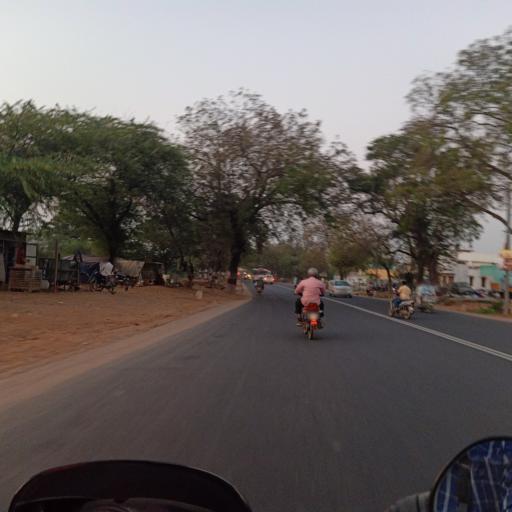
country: IN
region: Telangana
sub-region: Rangareddi
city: Secunderabad
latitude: 17.5476
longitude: 78.5353
